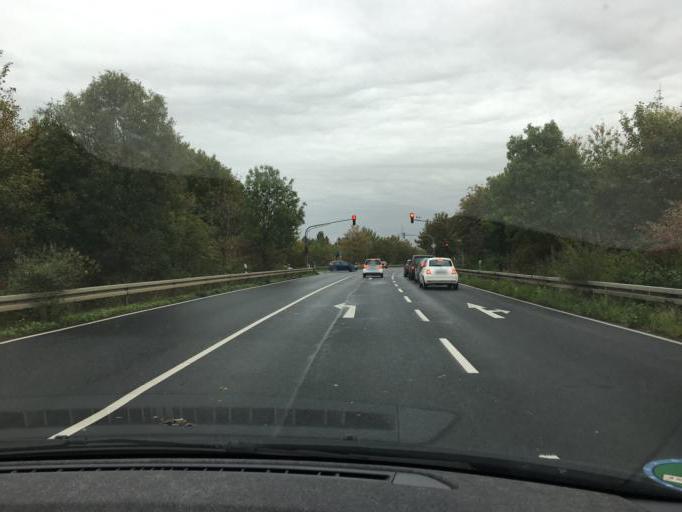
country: DE
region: North Rhine-Westphalia
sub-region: Regierungsbezirk Koln
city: Bergheim
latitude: 50.9373
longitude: 6.6130
